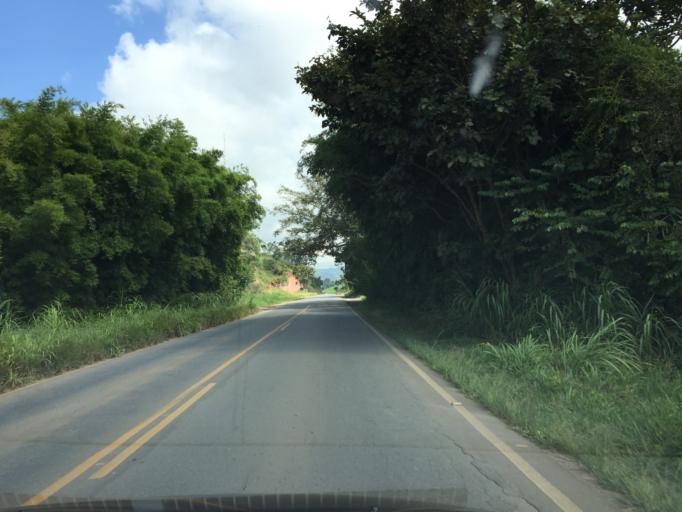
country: BR
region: Minas Gerais
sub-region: Passa Quatro
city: Passa Quatro
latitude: -22.3666
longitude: -44.9568
